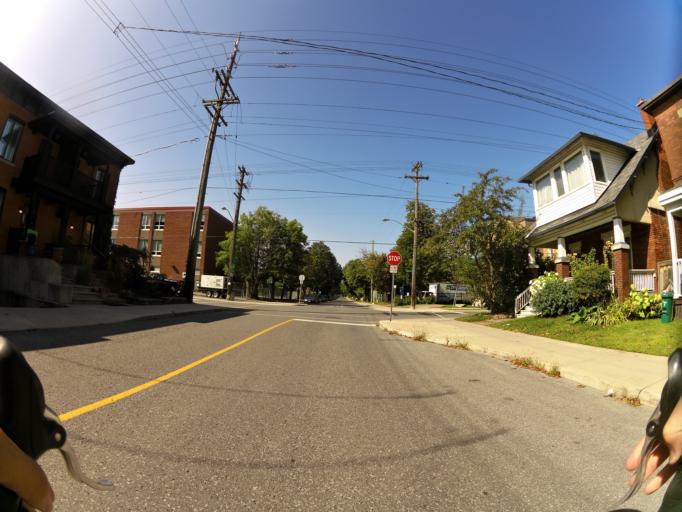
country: CA
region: Ontario
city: Ottawa
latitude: 45.4021
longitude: -75.6906
